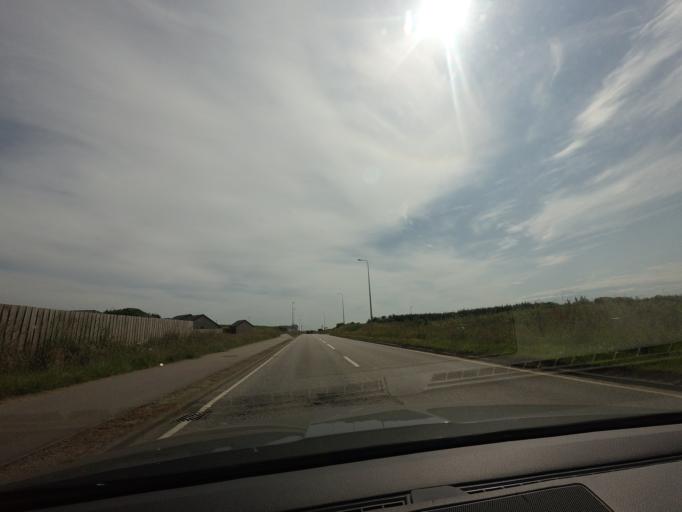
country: GB
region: Scotland
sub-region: Aberdeenshire
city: Peterhead
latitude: 57.5024
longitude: -1.8252
